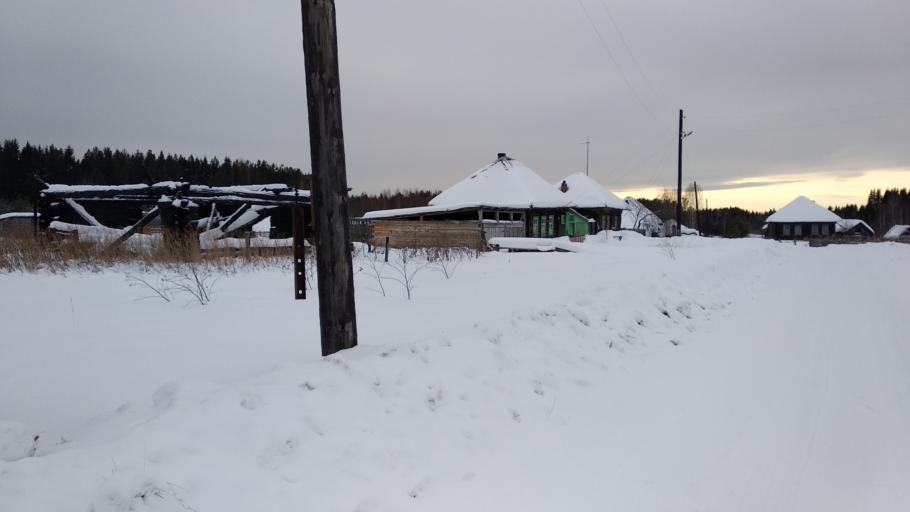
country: RU
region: Sverdlovsk
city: Krasnotur'insk
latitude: 60.0321
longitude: 60.4838
